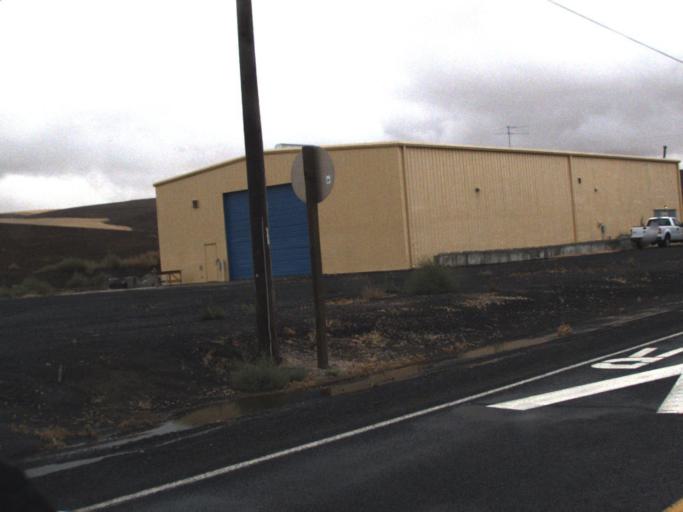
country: US
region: Washington
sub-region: Whitman County
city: Colfax
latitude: 47.0919
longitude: -117.5765
